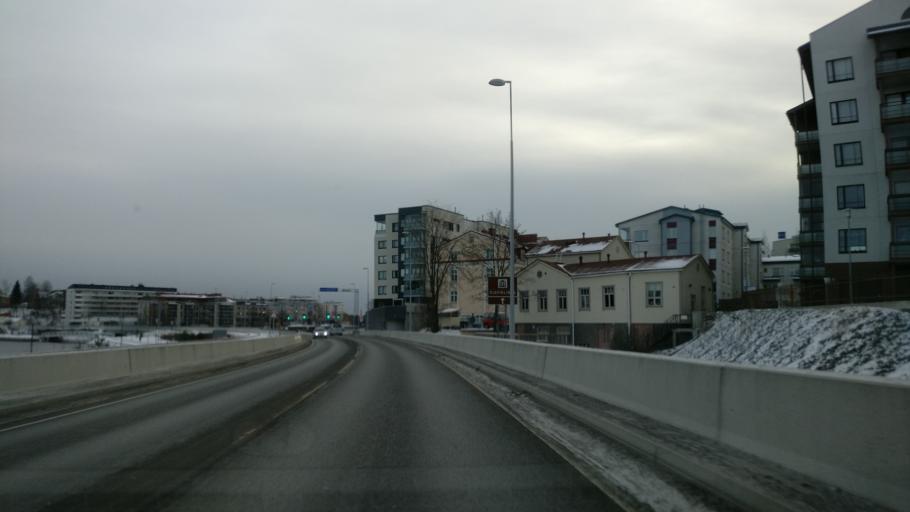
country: FI
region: Southern Savonia
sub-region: Savonlinna
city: Savonlinna
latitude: 61.8717
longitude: 28.8818
